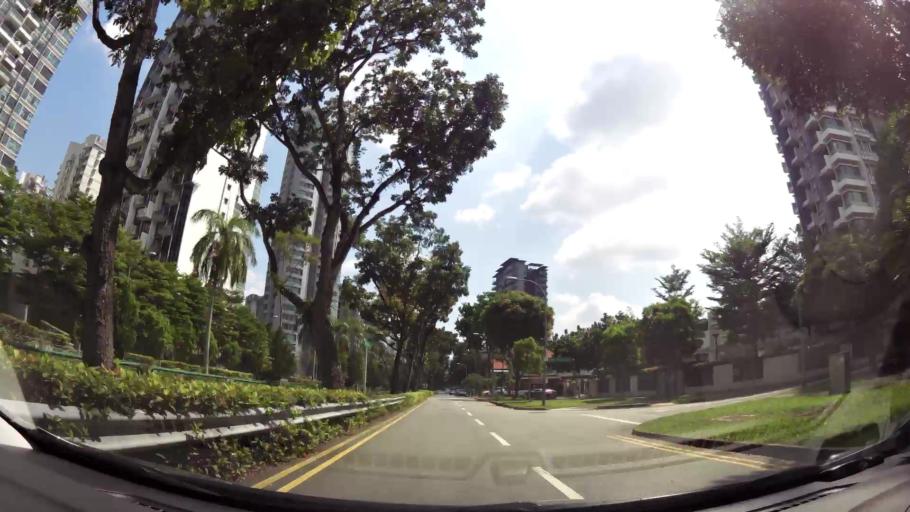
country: SG
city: Singapore
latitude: 1.3132
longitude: 103.8419
